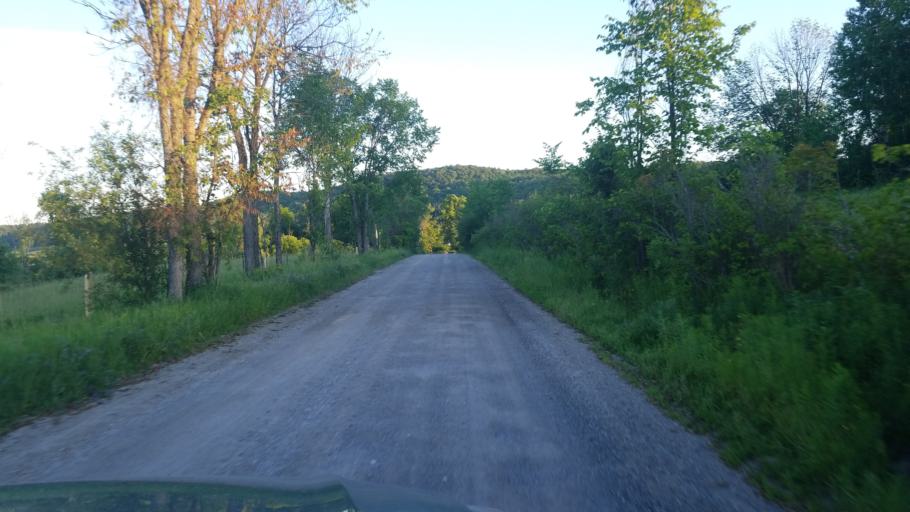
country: CA
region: Quebec
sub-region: Outaouais
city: Wakefield
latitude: 45.5877
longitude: -75.9031
